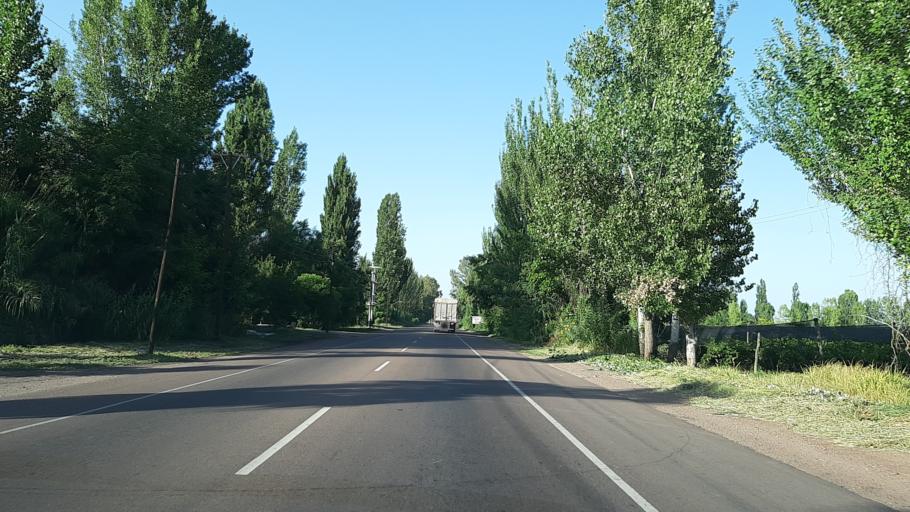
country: AR
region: Mendoza
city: San Martin
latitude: -33.0276
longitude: -68.5070
